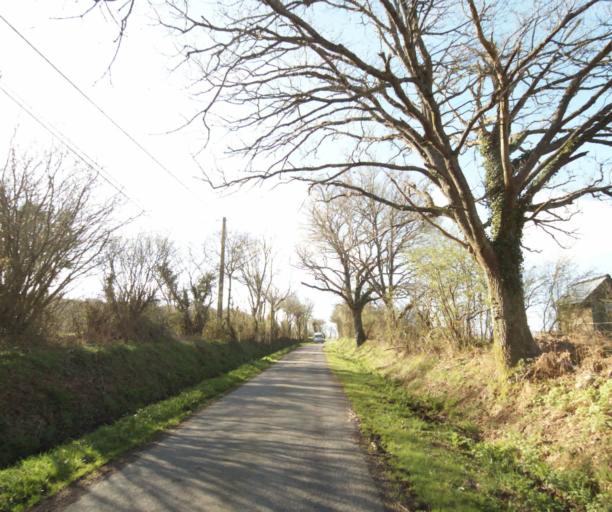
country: FR
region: Pays de la Loire
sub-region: Departement de la Loire-Atlantique
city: Bouvron
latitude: 47.4011
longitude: -1.8482
